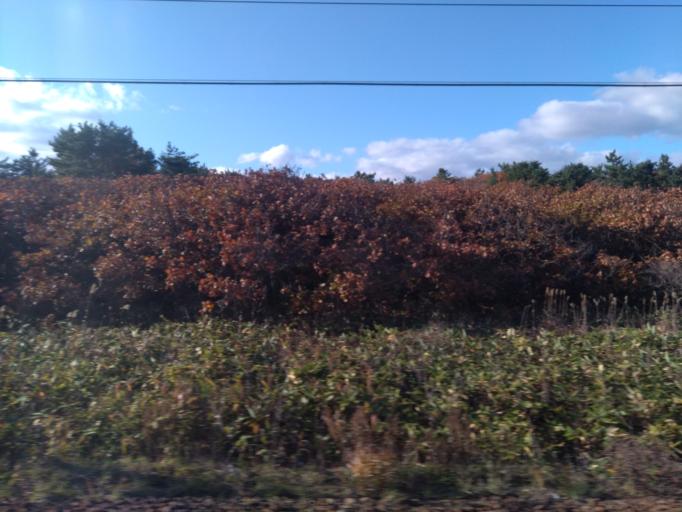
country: JP
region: Hokkaido
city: Niseko Town
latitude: 42.5540
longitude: 140.4219
